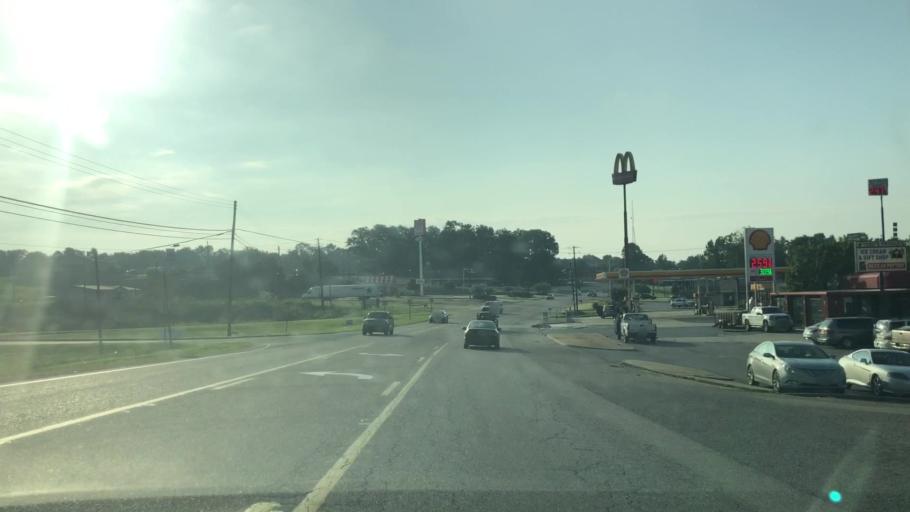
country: US
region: Alabama
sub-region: Chilton County
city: Clanton
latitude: 32.8013
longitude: -86.5773
